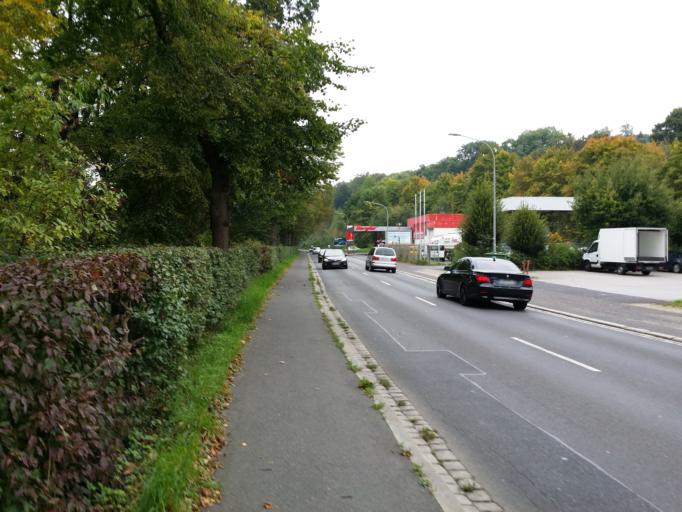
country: DE
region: Bavaria
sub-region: Upper Palatinate
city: Amberg
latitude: 49.4505
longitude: 11.8541
